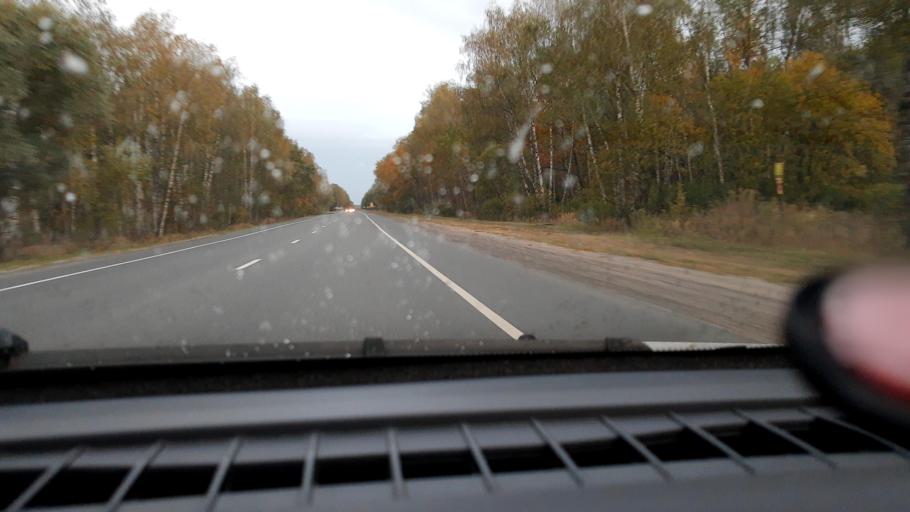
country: RU
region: Vladimir
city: Orgtrud
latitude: 56.2051
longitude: 40.7259
